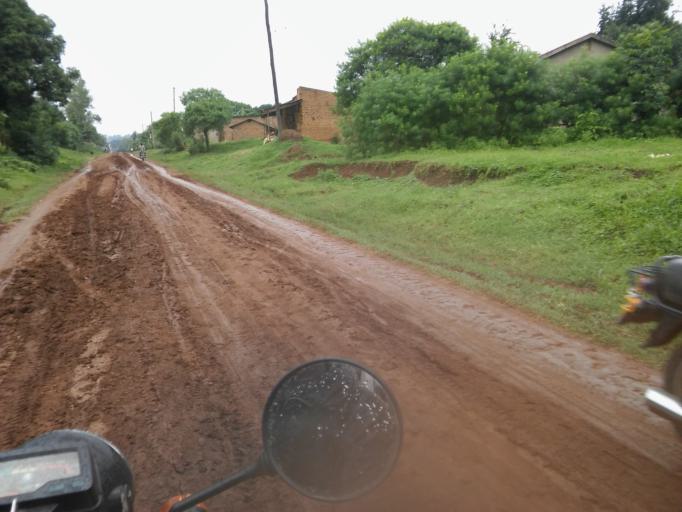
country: UG
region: Eastern Region
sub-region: Mbale District
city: Mbale
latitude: 1.0034
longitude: 34.1916
